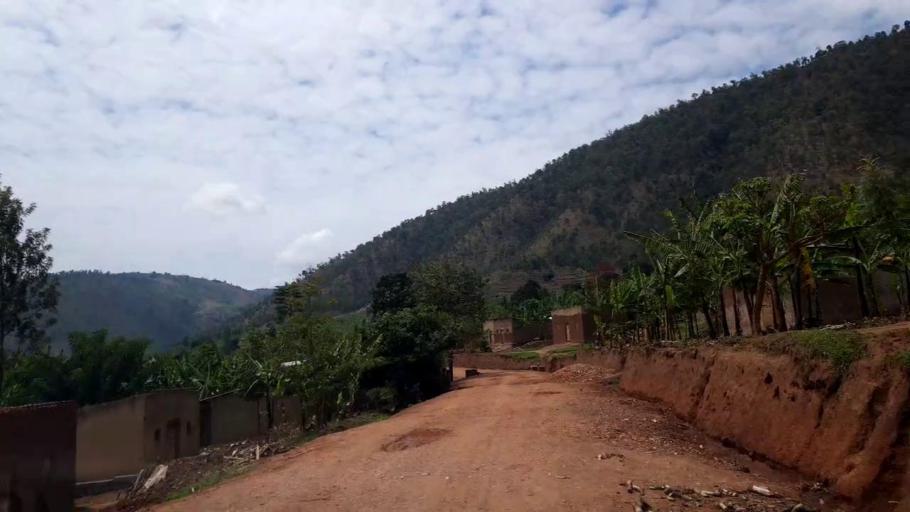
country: RW
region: Northern Province
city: Byumba
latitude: -1.5003
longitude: 30.1933
